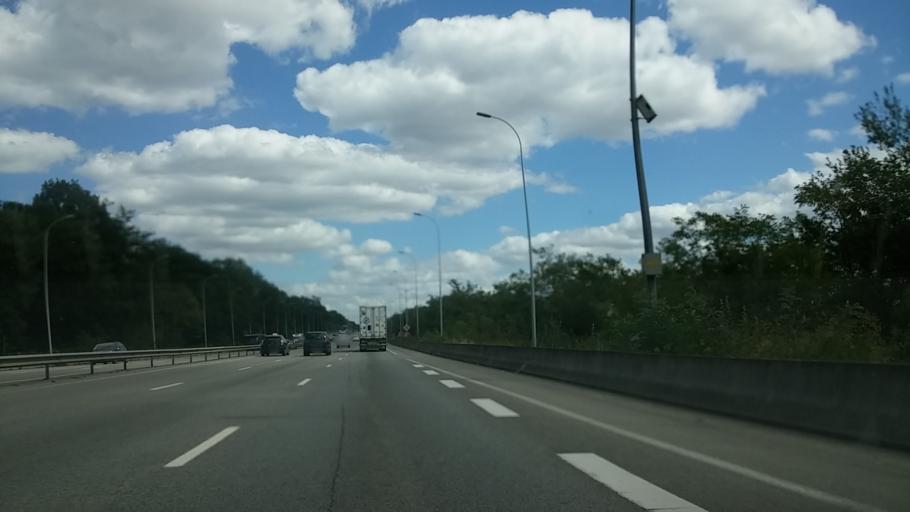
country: FR
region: Ile-de-France
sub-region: Departement des Yvelines
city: Saint-Cyr-l'Ecole
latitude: 48.7929
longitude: 2.0843
